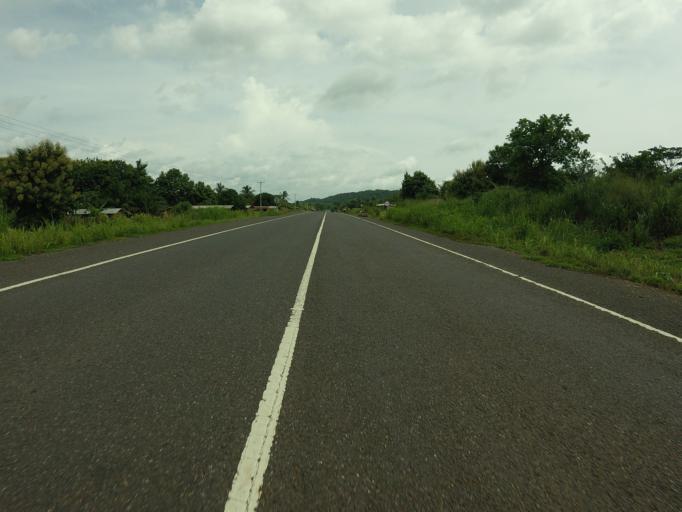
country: TG
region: Plateaux
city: Badou
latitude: 7.9548
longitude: 0.5549
